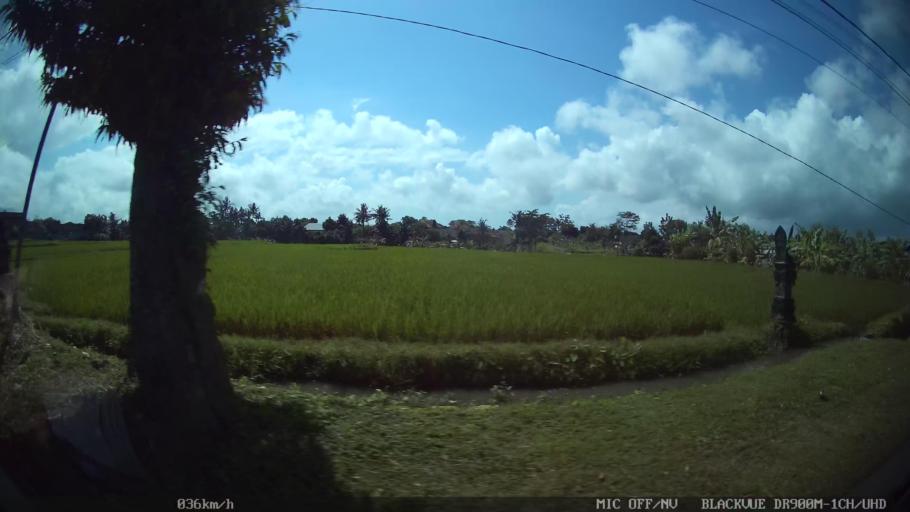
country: ID
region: Bali
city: Banjar Sedang
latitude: -8.5547
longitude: 115.2690
